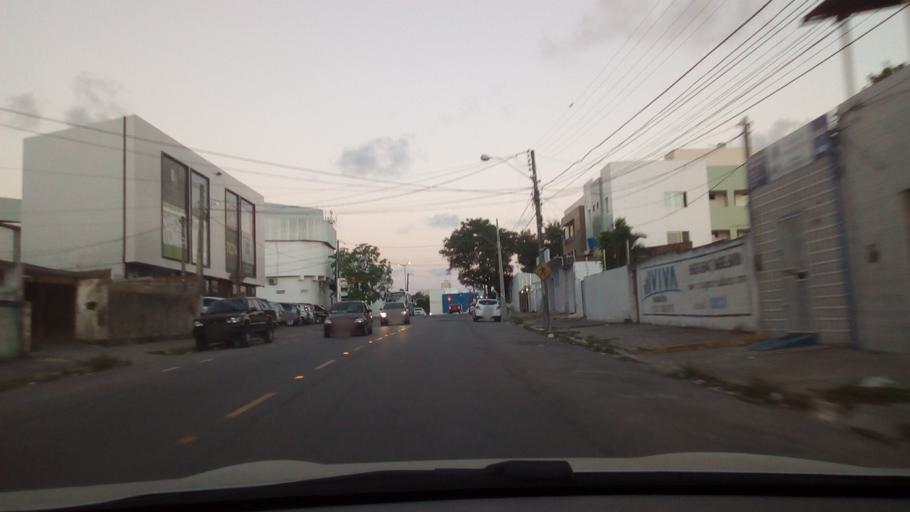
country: BR
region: Paraiba
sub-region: Joao Pessoa
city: Joao Pessoa
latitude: -7.1496
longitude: -34.8438
